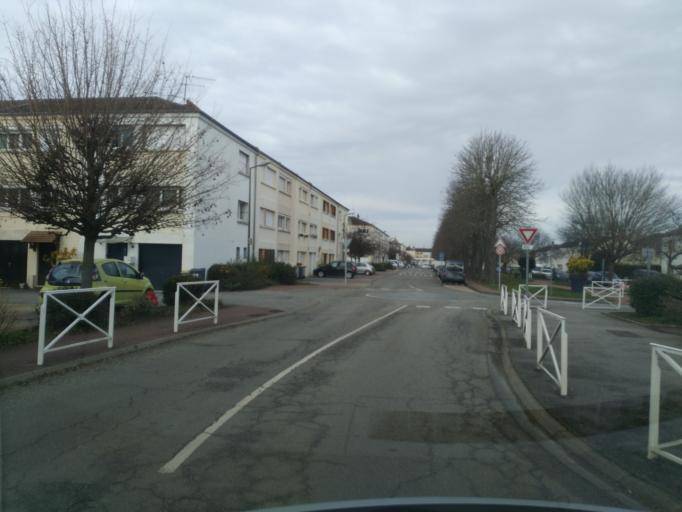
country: FR
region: Ile-de-France
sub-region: Departement des Yvelines
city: Villepreux
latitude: 48.8247
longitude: 2.0000
